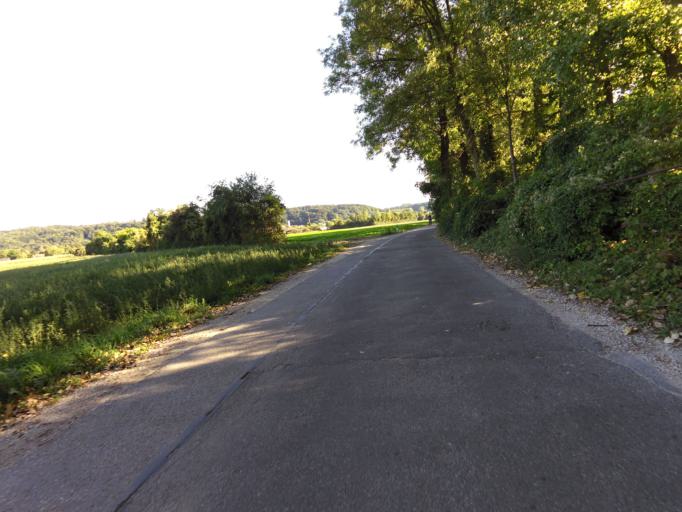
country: DE
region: Bavaria
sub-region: Lower Bavaria
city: Ergolding
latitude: 48.5632
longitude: 12.1951
